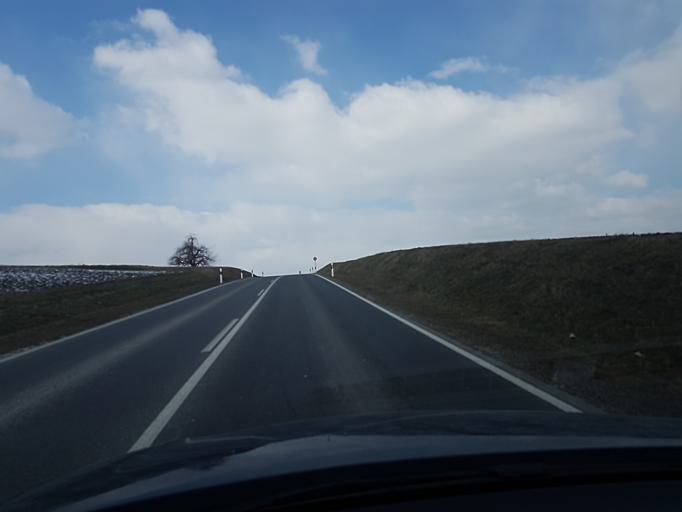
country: DE
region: Baden-Wuerttemberg
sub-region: Regierungsbezirk Stuttgart
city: Herrenberg
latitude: 48.5791
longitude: 8.8629
